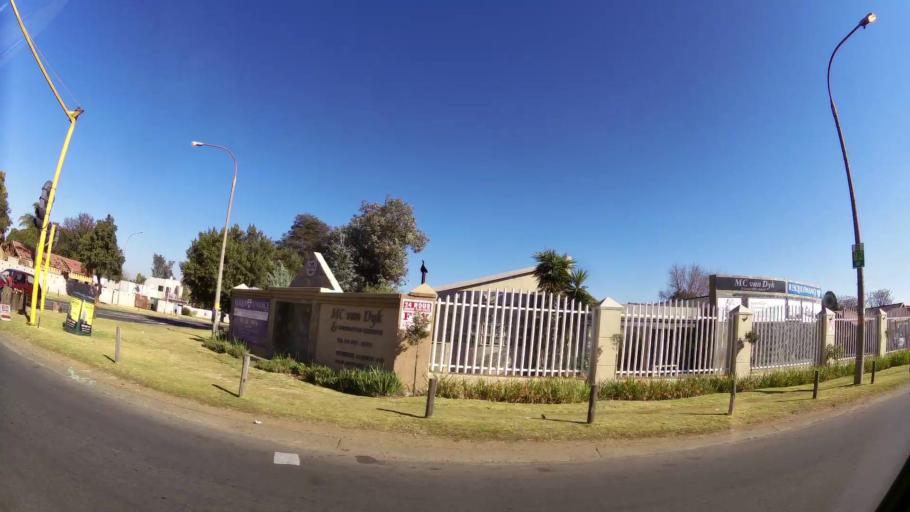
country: ZA
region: Gauteng
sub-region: Ekurhuleni Metropolitan Municipality
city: Germiston
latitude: -26.3162
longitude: 28.0963
